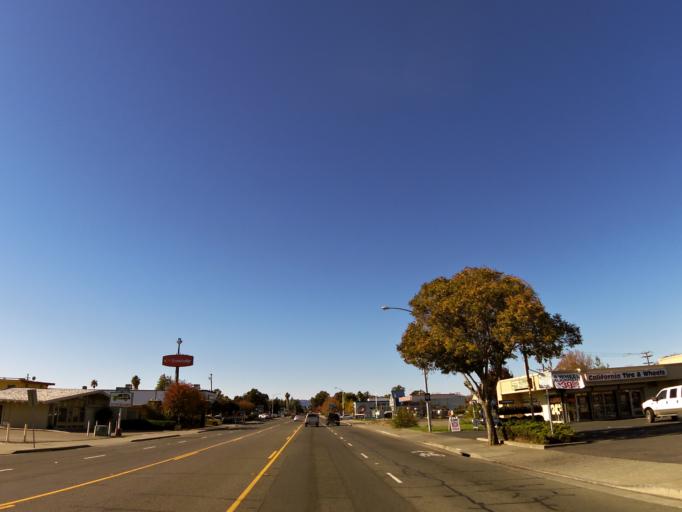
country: US
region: California
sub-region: Solano County
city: Fairfield
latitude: 38.2493
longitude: -122.0514
